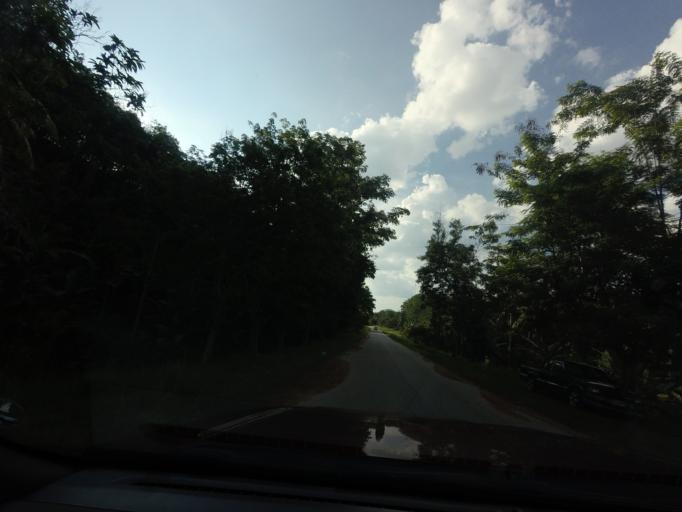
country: TH
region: Yala
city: Ban Nang Sata
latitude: 6.2085
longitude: 101.2347
